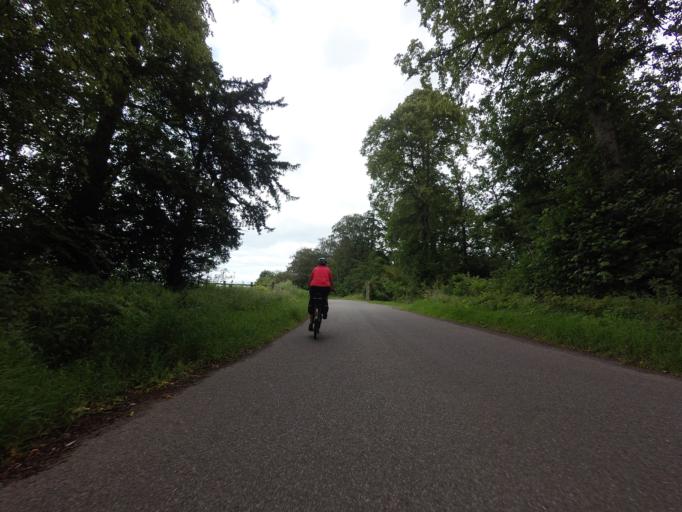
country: GB
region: Scotland
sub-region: Moray
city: Forres
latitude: 57.6184
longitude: -3.6526
